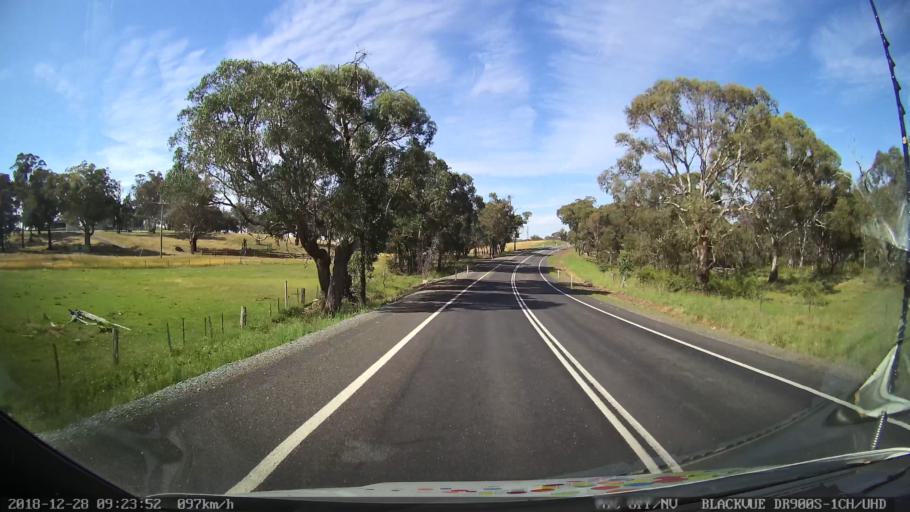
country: AU
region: New South Wales
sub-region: Upper Lachlan Shire
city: Crookwell
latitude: -34.3911
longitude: 149.3839
